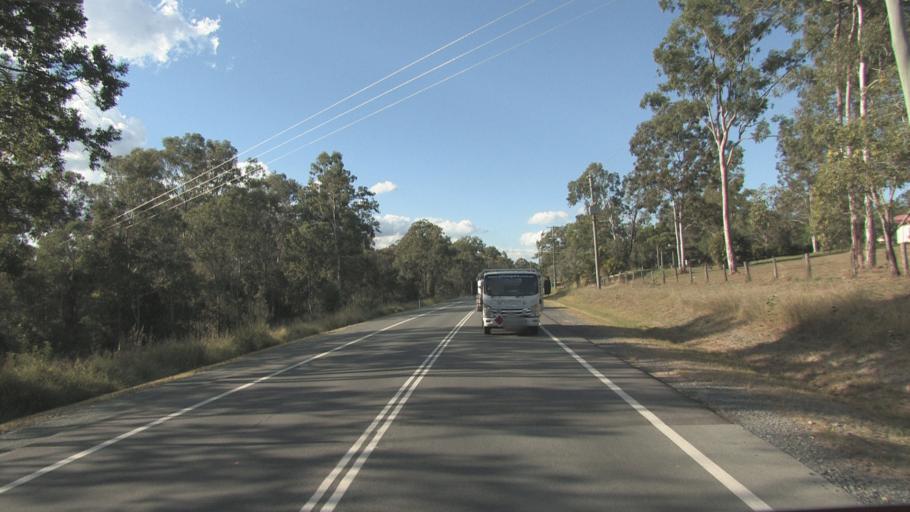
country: AU
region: Queensland
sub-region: Ipswich
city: Springfield Lakes
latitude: -27.7252
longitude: 152.9573
